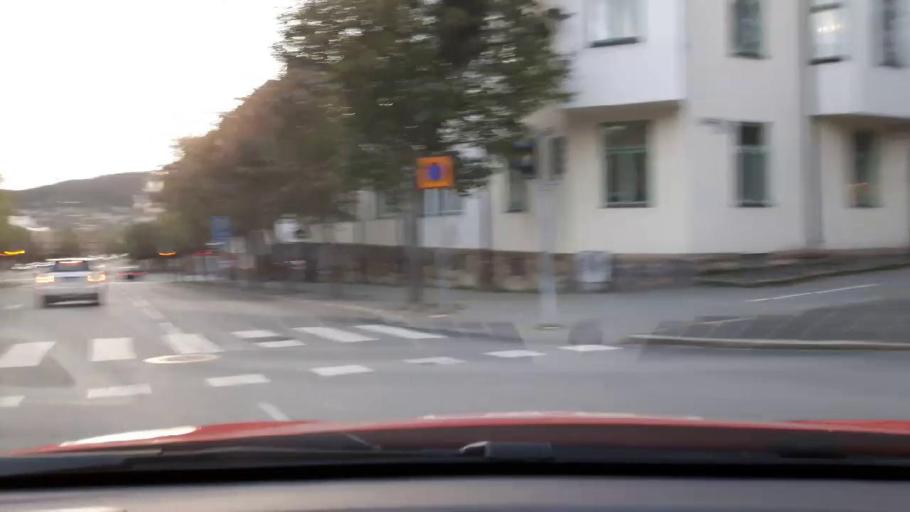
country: SE
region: Jaemtland
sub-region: OEstersunds Kommun
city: Ostersund
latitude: 63.1807
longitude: 14.6399
